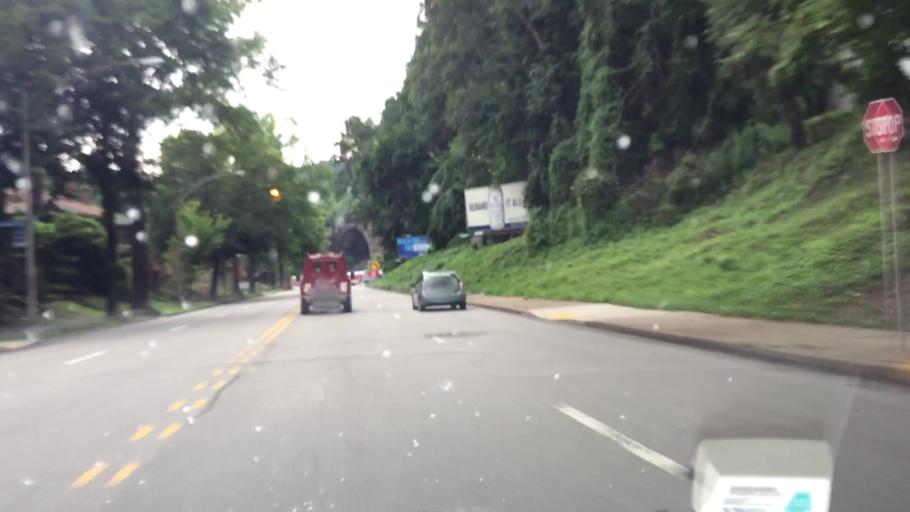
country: US
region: Pennsylvania
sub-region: Allegheny County
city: Wilkinsburg
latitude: 40.4599
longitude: -79.9071
